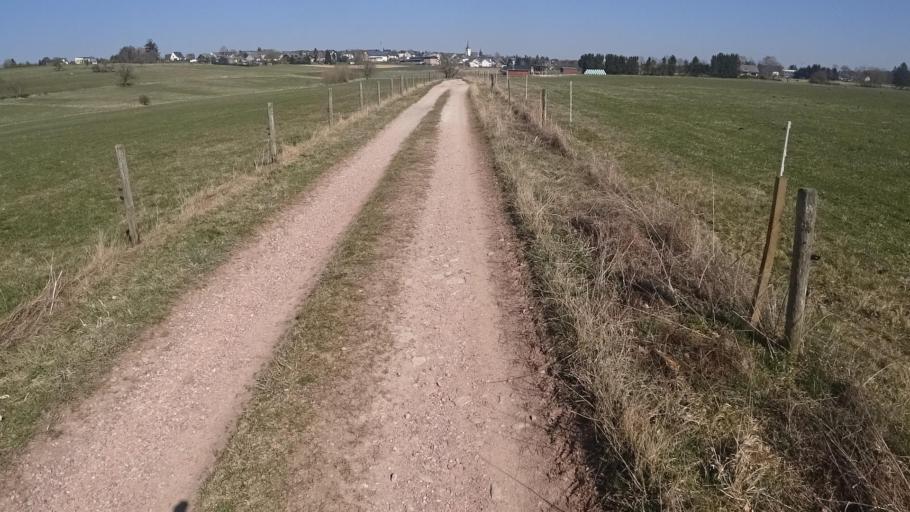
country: DE
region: Rheinland-Pfalz
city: Argenthal
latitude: 49.9694
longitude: 7.5874
